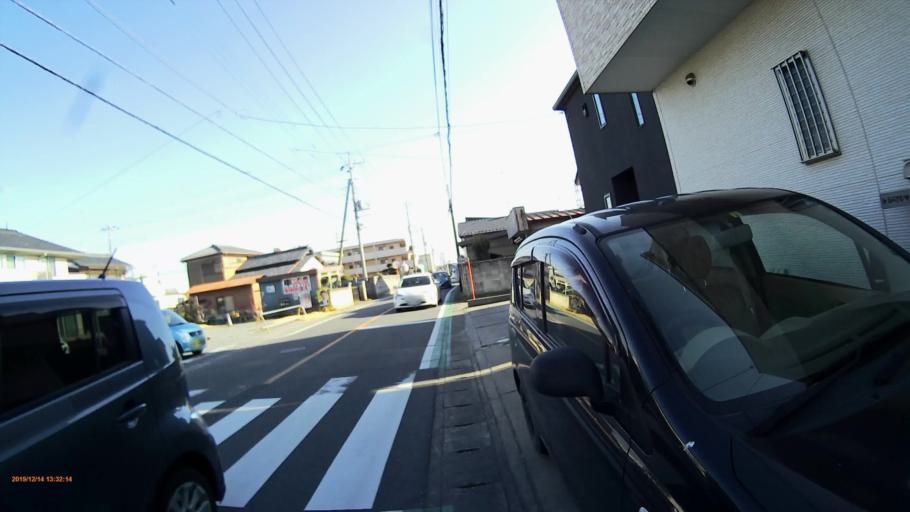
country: JP
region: Saitama
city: Konosu
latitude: 36.0778
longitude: 139.4817
